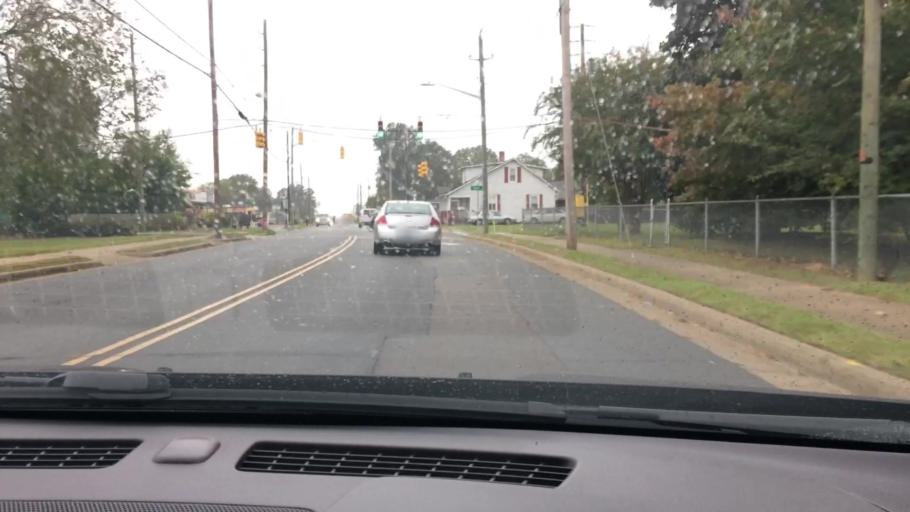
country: US
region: North Carolina
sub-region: Pitt County
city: Greenville
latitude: 35.6129
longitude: -77.3862
